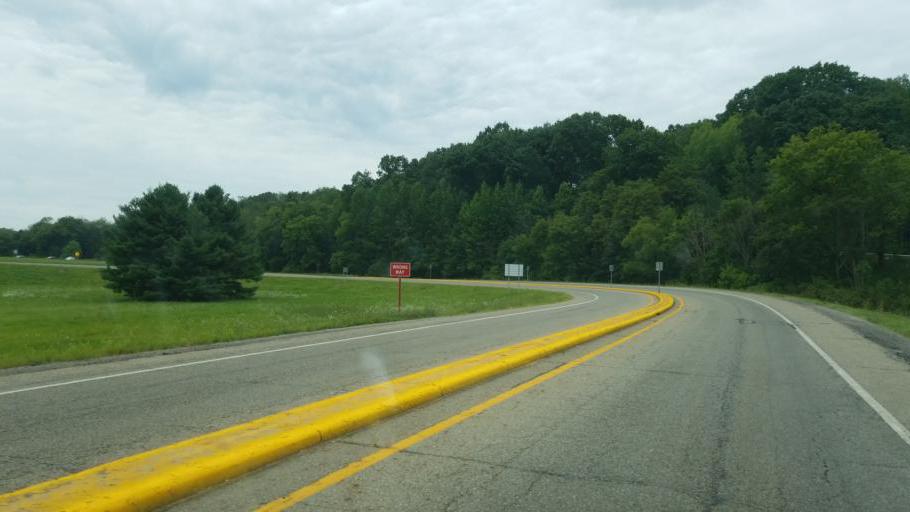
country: US
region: Ohio
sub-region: Columbiana County
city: Lisbon
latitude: 40.7668
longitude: -80.7254
